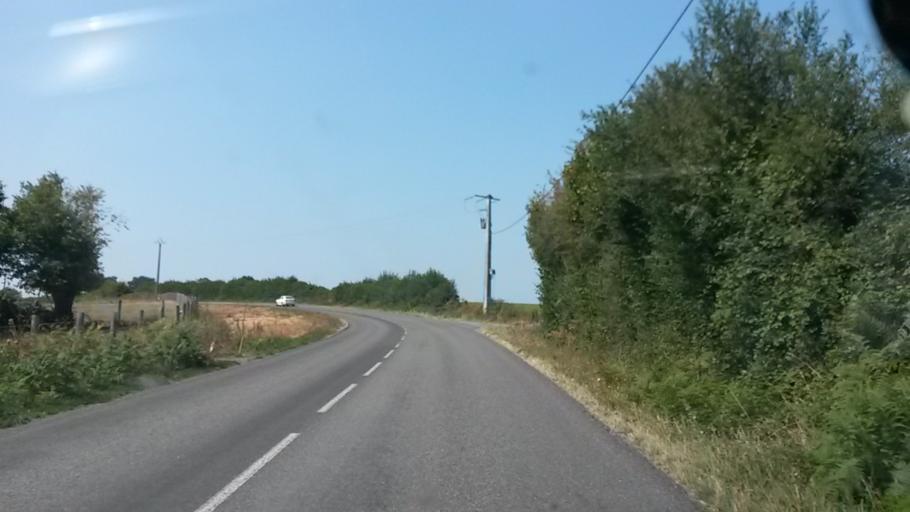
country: FR
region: Pays de la Loire
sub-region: Departement de la Mayenne
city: Saint-Pierre-des-Nids
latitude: 48.3889
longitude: -0.1302
